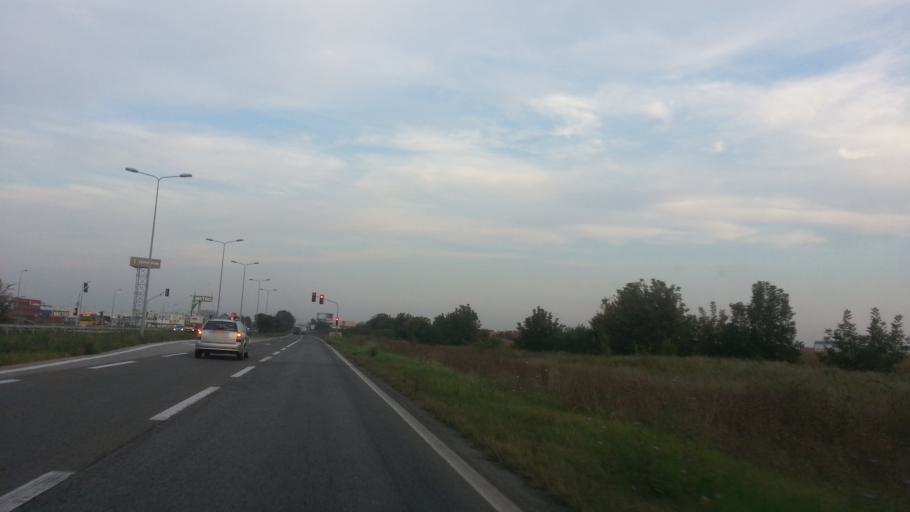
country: RS
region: Central Serbia
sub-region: Belgrade
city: Zemun
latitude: 44.8675
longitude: 20.3415
